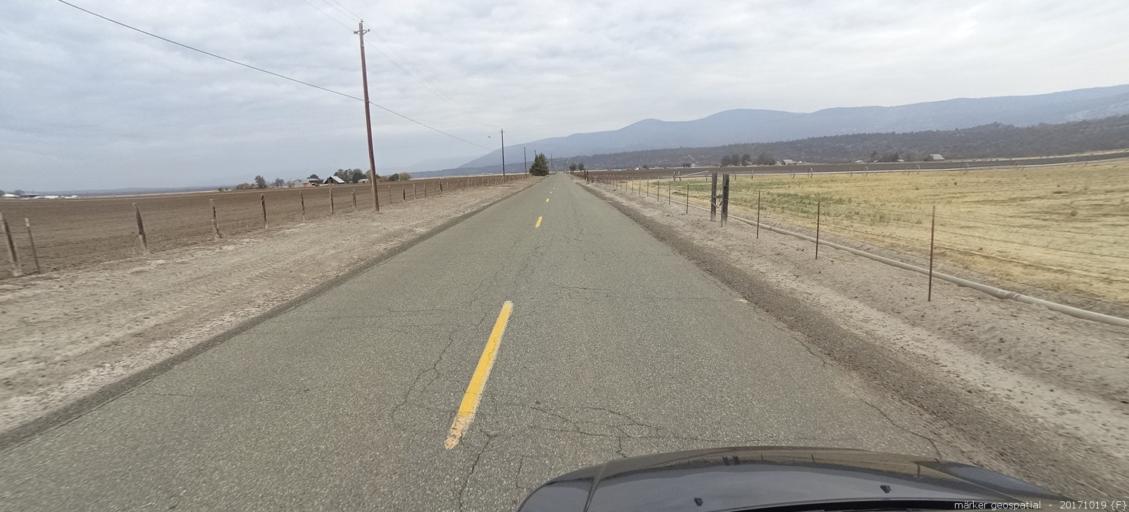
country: US
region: California
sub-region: Shasta County
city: Burney
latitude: 41.0741
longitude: -121.3314
